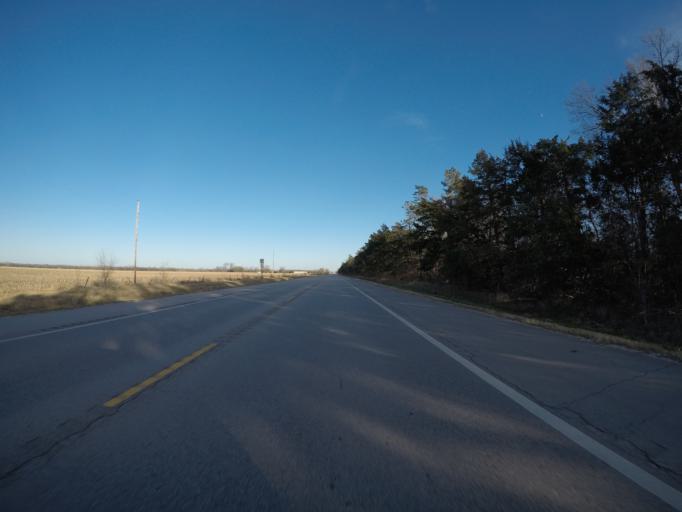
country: US
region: Kansas
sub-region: Harvey County
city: Halstead
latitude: 38.0286
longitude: -97.5549
